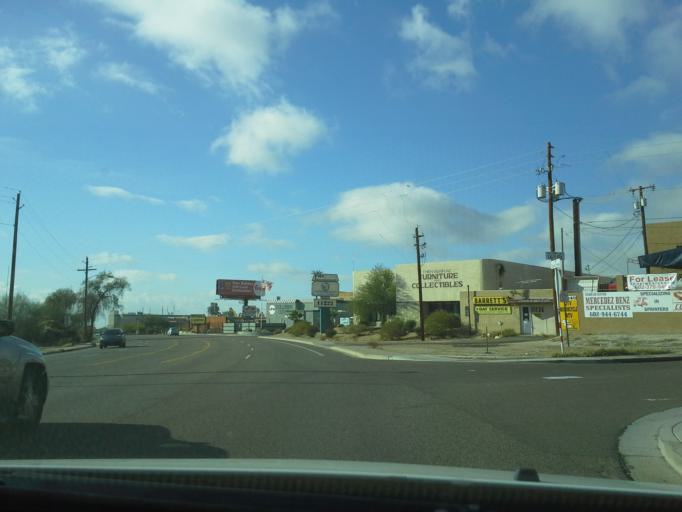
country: US
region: Arizona
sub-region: Maricopa County
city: Paradise Valley
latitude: 33.5892
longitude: -112.0473
